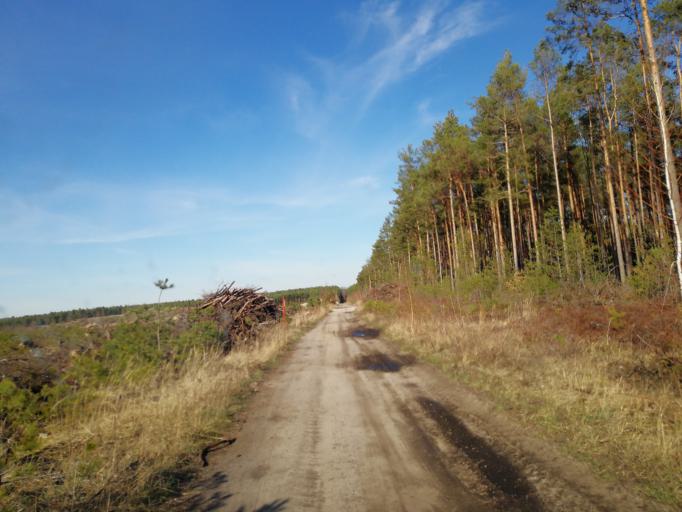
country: DE
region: Brandenburg
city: Ruckersdorf
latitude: 51.5711
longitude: 13.5951
